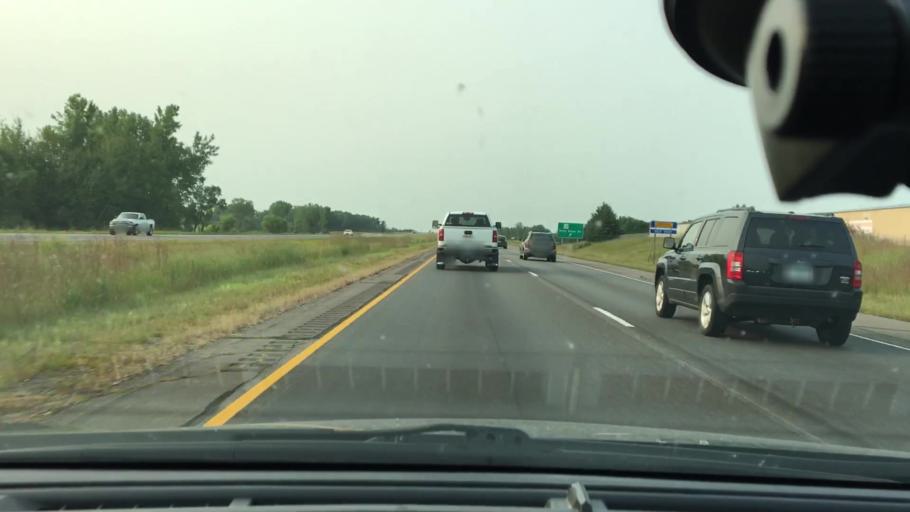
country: US
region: Minnesota
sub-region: Mille Lacs County
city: Princeton
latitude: 45.5877
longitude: -93.6004
